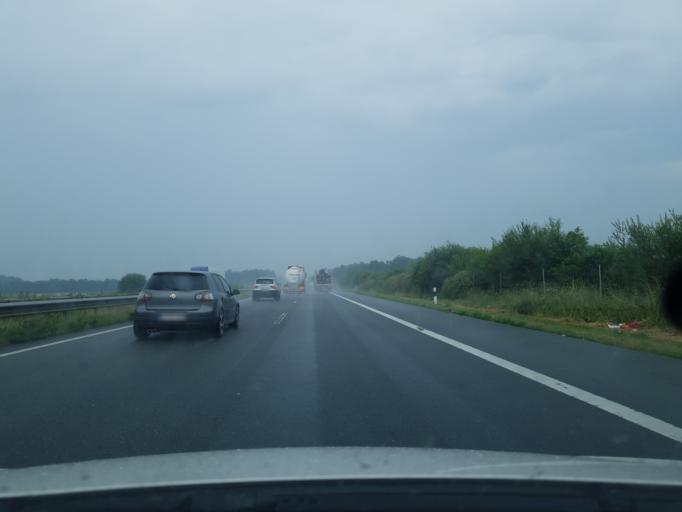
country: DE
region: North Rhine-Westphalia
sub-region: Regierungsbezirk Munster
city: Ochtrup
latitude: 52.2585
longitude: 7.1730
